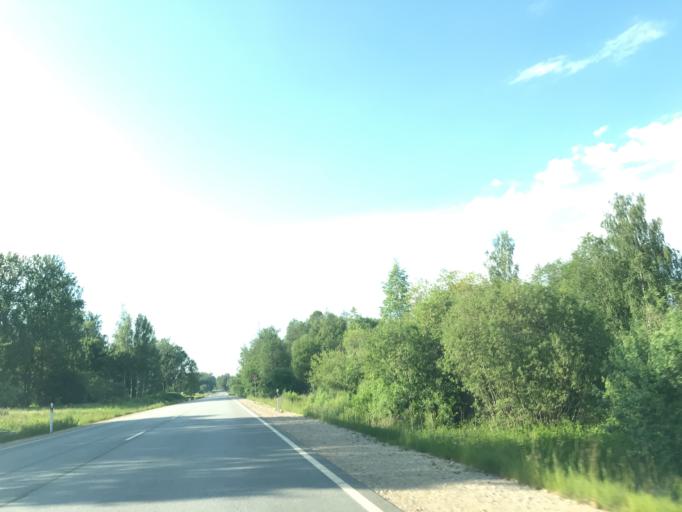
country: LV
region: Ogre
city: Jumprava
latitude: 56.6466
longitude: 24.8829
